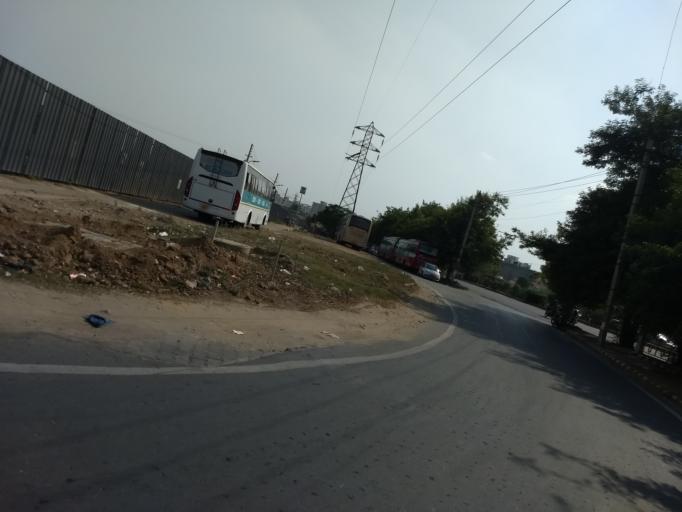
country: IN
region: Haryana
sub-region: Gurgaon
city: Gurgaon
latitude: 28.4343
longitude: 77.0493
